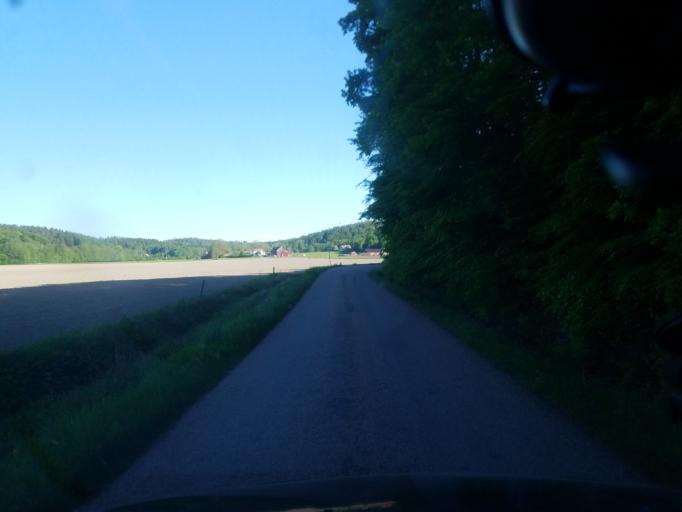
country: SE
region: Vaestra Goetaland
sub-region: Orust
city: Henan
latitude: 58.2854
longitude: 11.6401
